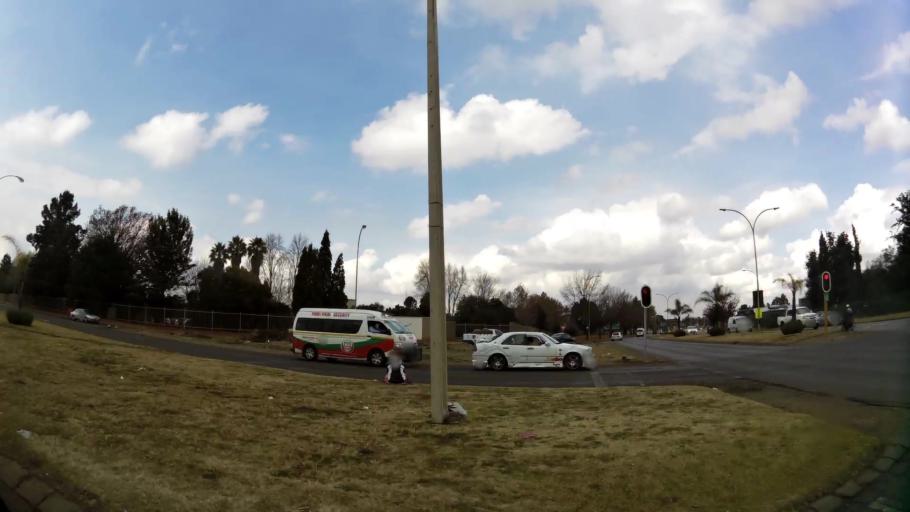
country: ZA
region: Gauteng
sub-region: Sedibeng District Municipality
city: Vanderbijlpark
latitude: -26.7033
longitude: 27.8354
